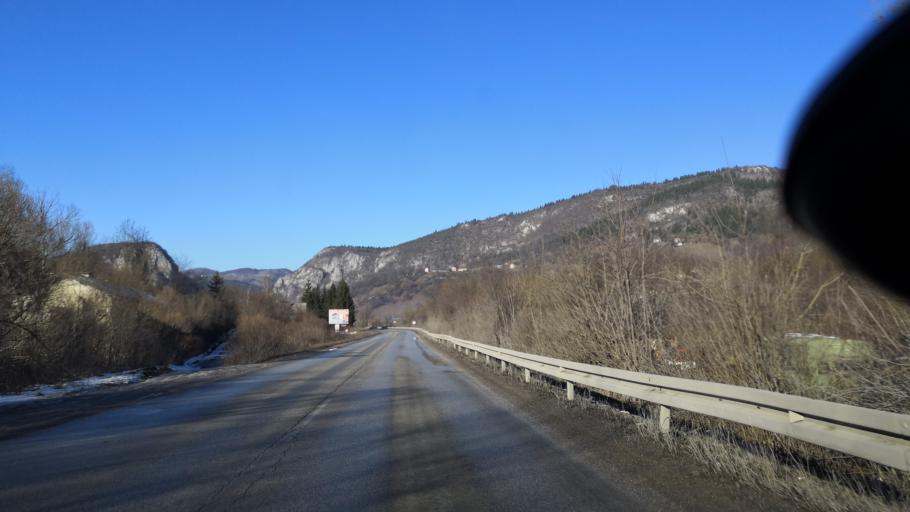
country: BA
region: Republika Srpska
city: Pale
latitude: 43.8430
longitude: 18.5518
